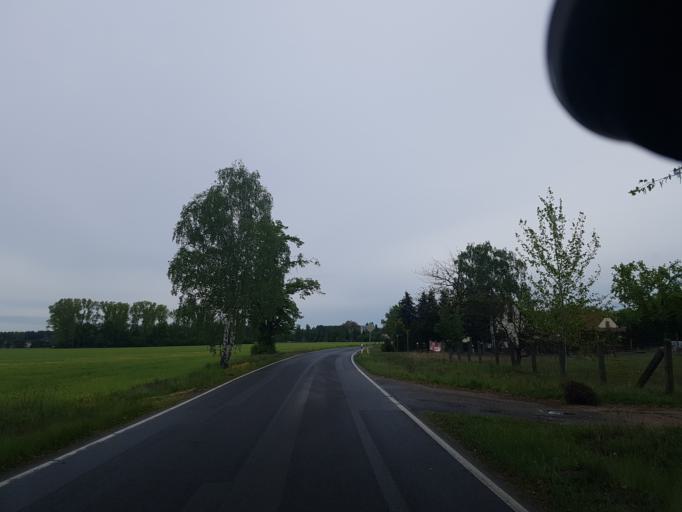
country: DE
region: Brandenburg
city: Spremberg
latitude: 51.6681
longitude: 14.4406
